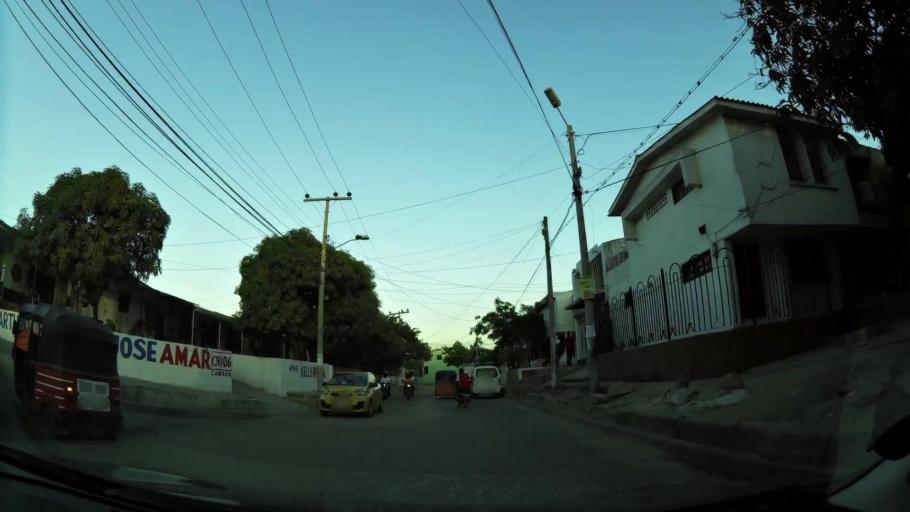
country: CO
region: Atlantico
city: Soledad
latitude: 10.9248
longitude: -74.7843
